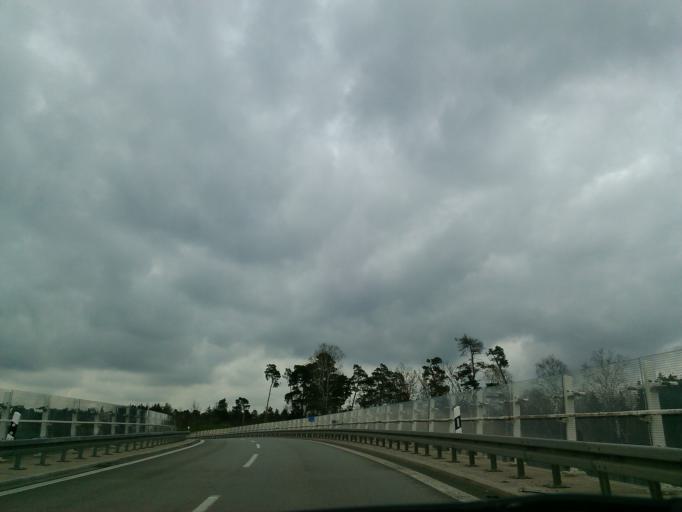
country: DE
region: Bavaria
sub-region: Upper Bavaria
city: Grafelfing
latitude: 48.1302
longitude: 11.4140
